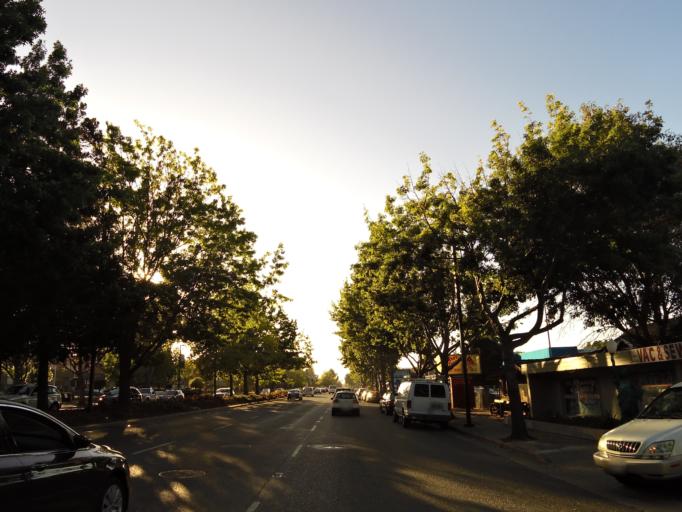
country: US
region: California
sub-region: Santa Clara County
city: Los Altos
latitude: 37.3949
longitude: -122.0998
